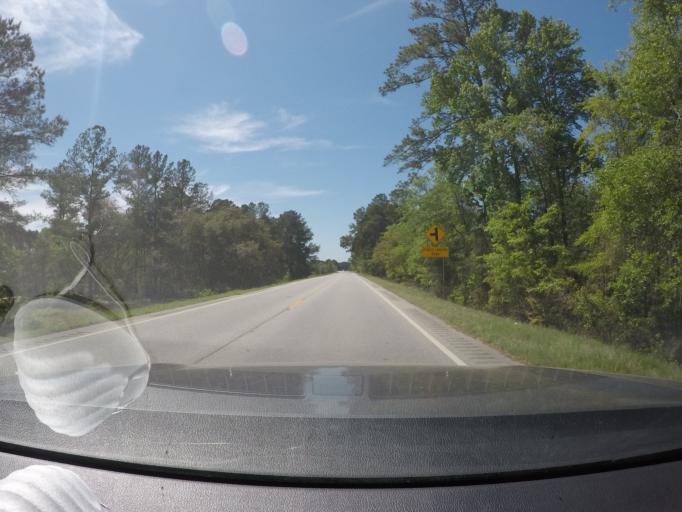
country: US
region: Georgia
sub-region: Evans County
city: Claxton
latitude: 32.1478
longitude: -81.7749
